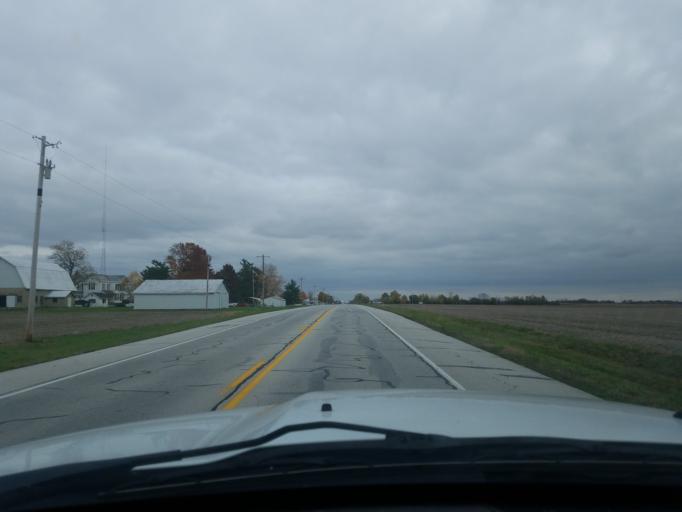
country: US
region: Indiana
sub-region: Johnson County
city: Franklin
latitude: 39.4953
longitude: -85.9270
